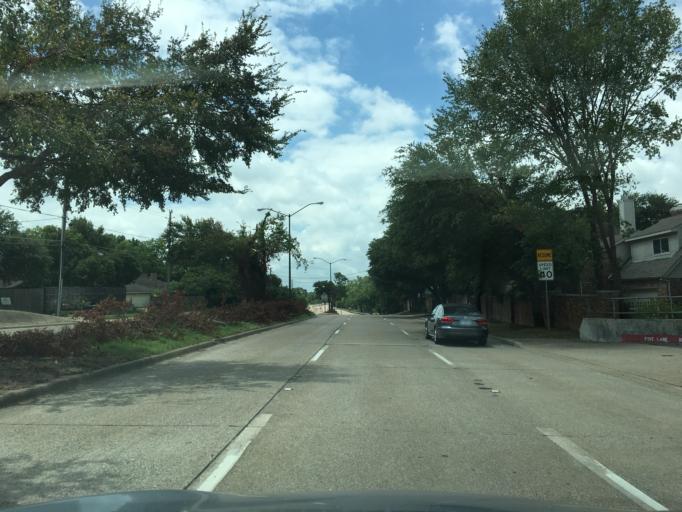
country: US
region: Texas
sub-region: Dallas County
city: University Park
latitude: 32.8778
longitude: -96.7417
